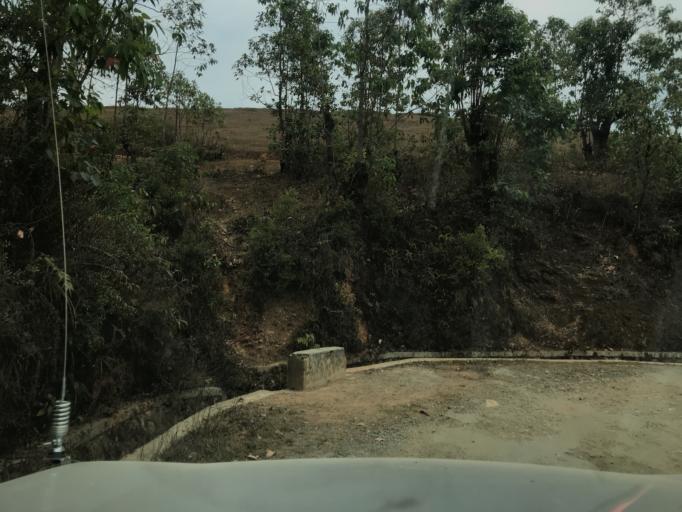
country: TL
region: Ermera
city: Gleno
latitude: -8.8380
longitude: 125.4371
